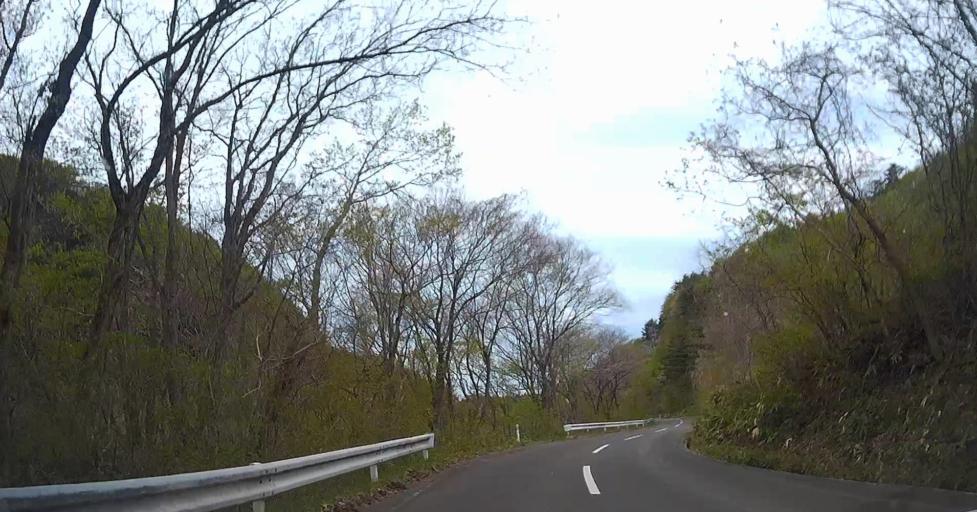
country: JP
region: Aomori
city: Goshogawara
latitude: 40.9046
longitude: 140.5064
